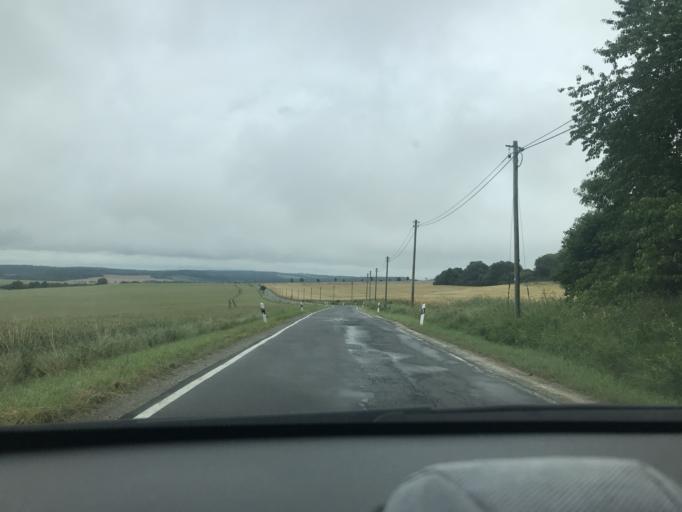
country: DE
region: Thuringia
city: Geisleden
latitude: 51.3225
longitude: 10.1925
